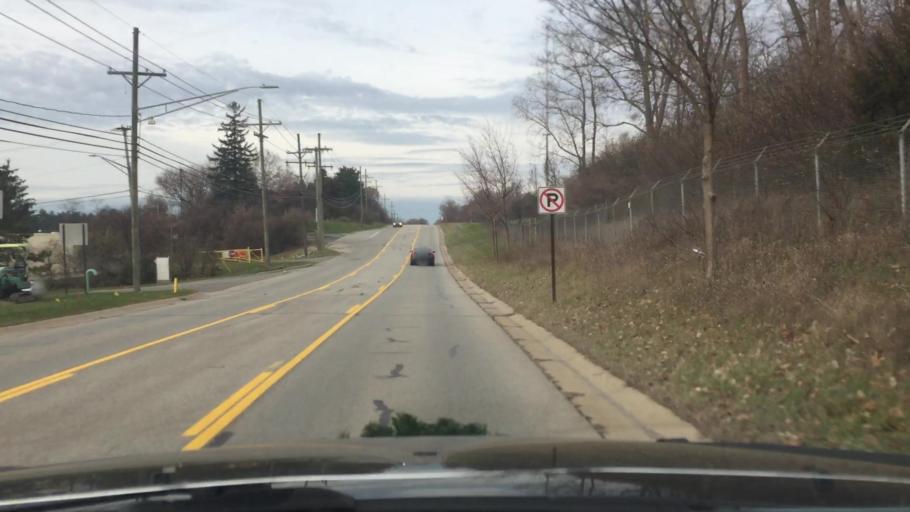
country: US
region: Michigan
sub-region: Oakland County
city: Auburn Hills
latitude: 42.7006
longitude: -83.2456
